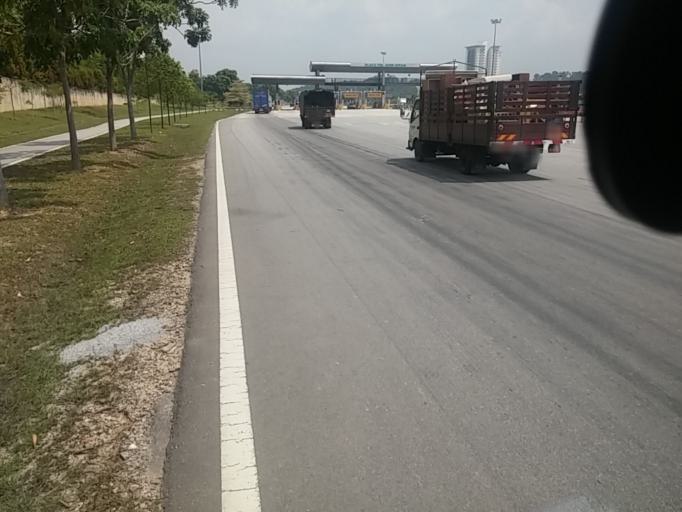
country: MY
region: Putrajaya
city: Putrajaya
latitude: 2.9760
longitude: 101.6531
